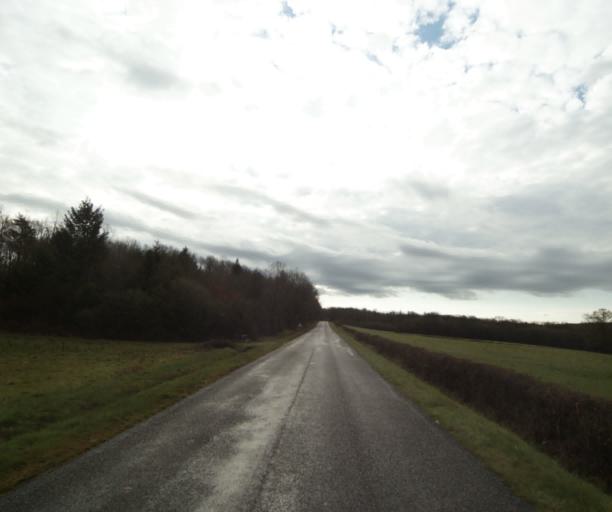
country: FR
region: Auvergne
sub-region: Departement de l'Allier
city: Neuilly-le-Real
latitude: 46.5201
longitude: 3.4223
